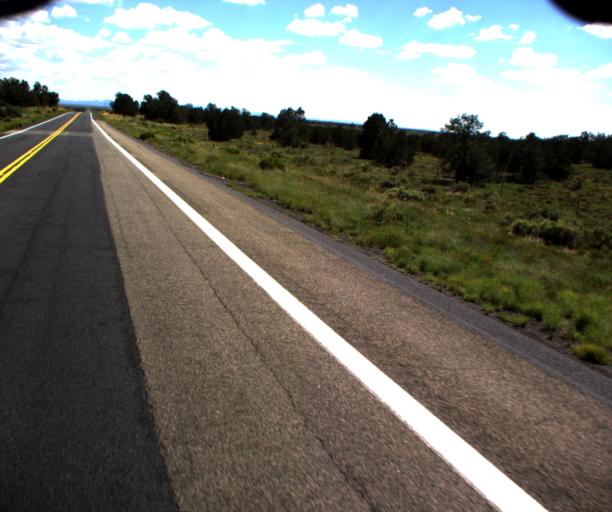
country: US
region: Arizona
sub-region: Coconino County
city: Grand Canyon Village
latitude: 35.8128
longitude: -112.1316
